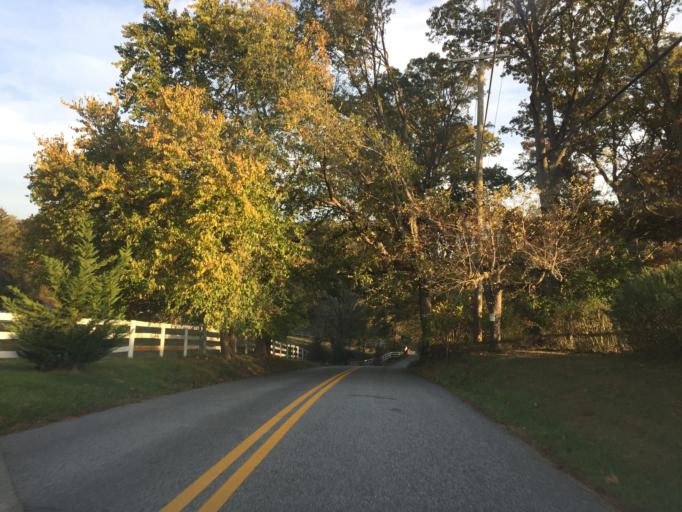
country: US
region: Maryland
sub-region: Baltimore County
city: Hampton
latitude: 39.4887
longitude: -76.5549
